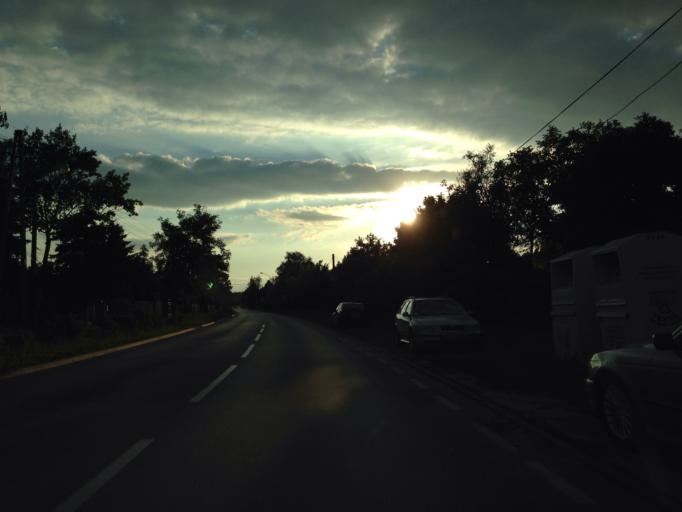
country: PL
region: Masovian Voivodeship
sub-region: Warszawa
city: Bemowo
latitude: 52.2477
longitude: 20.8826
